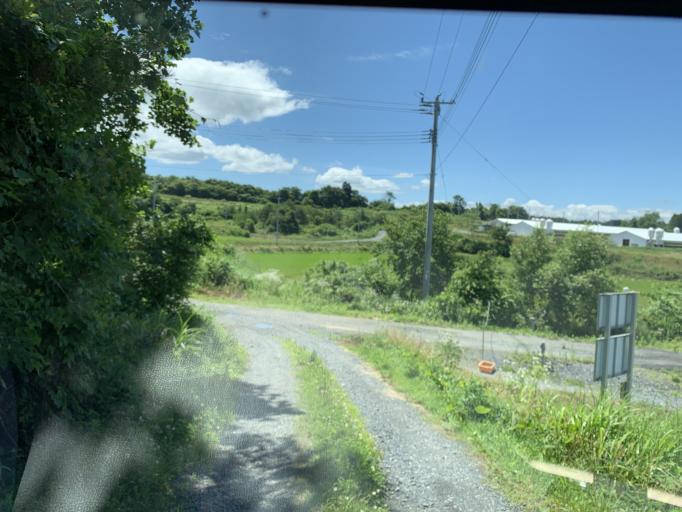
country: JP
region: Iwate
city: Ichinoseki
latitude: 38.9218
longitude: 141.0650
